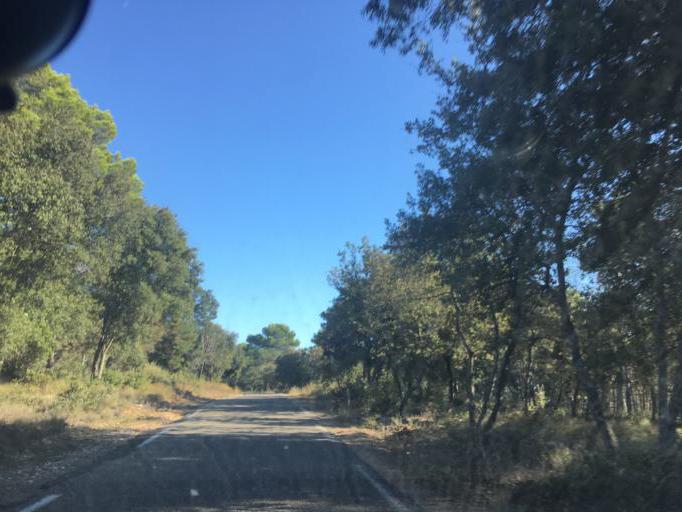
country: FR
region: Provence-Alpes-Cote d'Azur
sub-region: Departement du Var
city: Regusse
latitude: 43.7324
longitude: 6.1091
